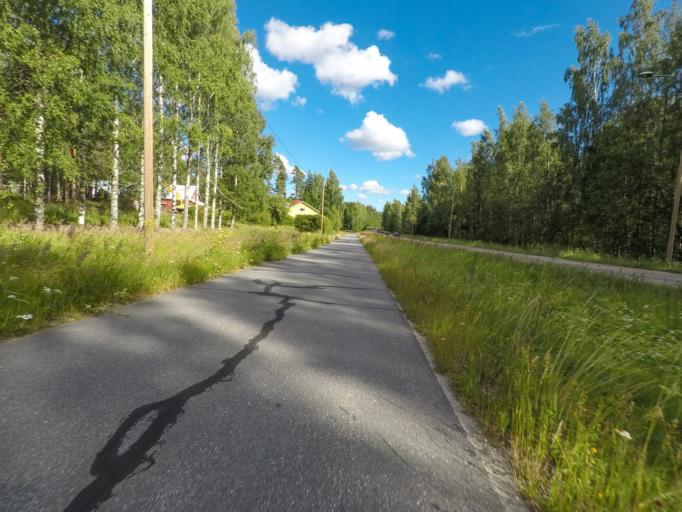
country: FI
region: South Karelia
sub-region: Lappeenranta
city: Taipalsaari
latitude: 61.1066
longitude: 28.1174
